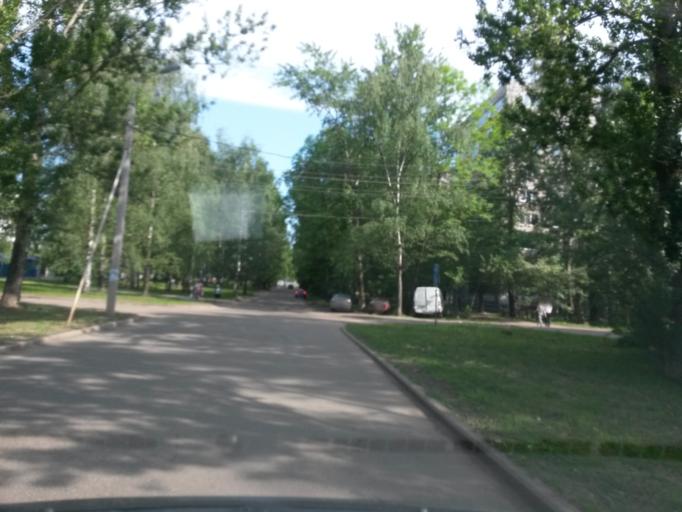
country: RU
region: Jaroslavl
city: Yaroslavl
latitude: 57.6925
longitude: 39.7717
